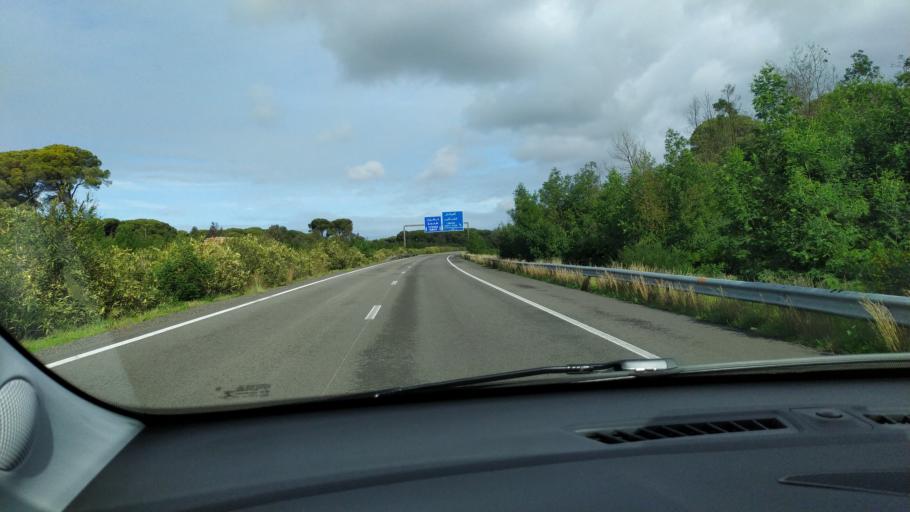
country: MA
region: Tanger-Tetouan
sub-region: Larache
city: Larache
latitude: 35.1328
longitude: -6.1469
